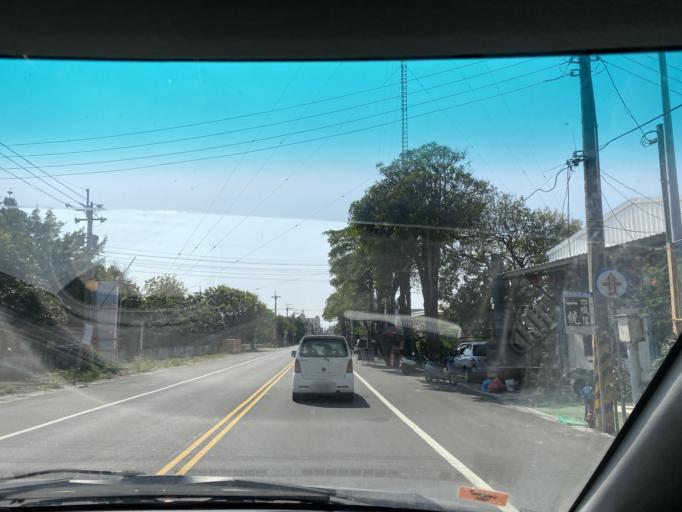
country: TW
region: Taiwan
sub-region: Changhua
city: Chang-hua
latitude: 23.9028
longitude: 120.3775
